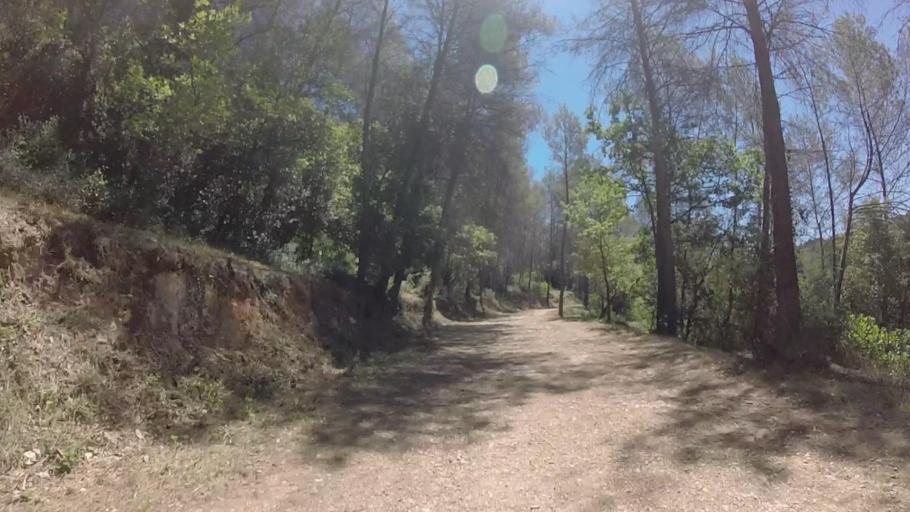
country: FR
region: Provence-Alpes-Cote d'Azur
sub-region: Departement des Alpes-Maritimes
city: Valbonne
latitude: 43.6353
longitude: 7.0386
